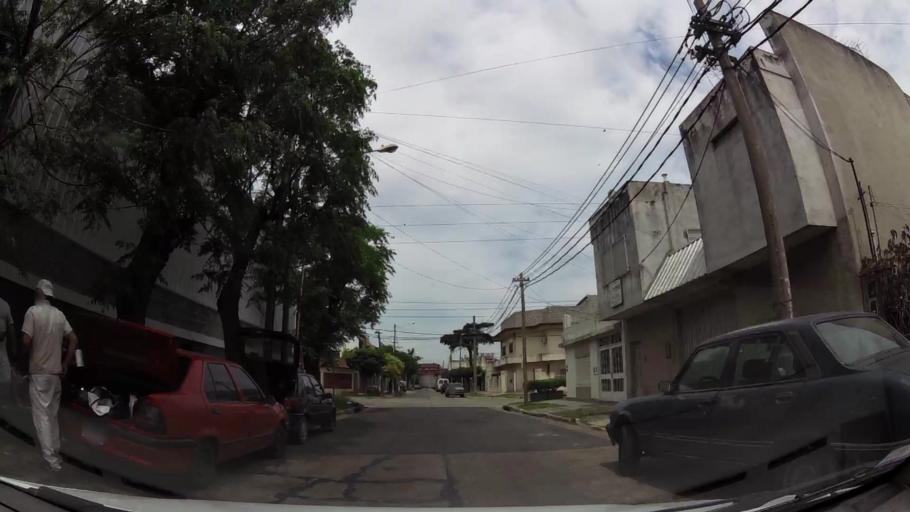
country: AR
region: Buenos Aires
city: San Justo
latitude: -34.6733
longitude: -58.5342
